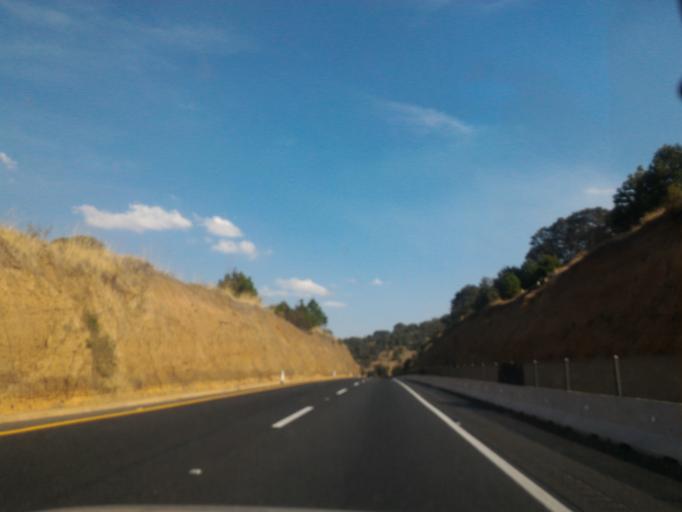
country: MX
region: Mexico
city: Temascalcingo de Jose Maria Velazco
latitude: 19.8530
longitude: -100.0184
